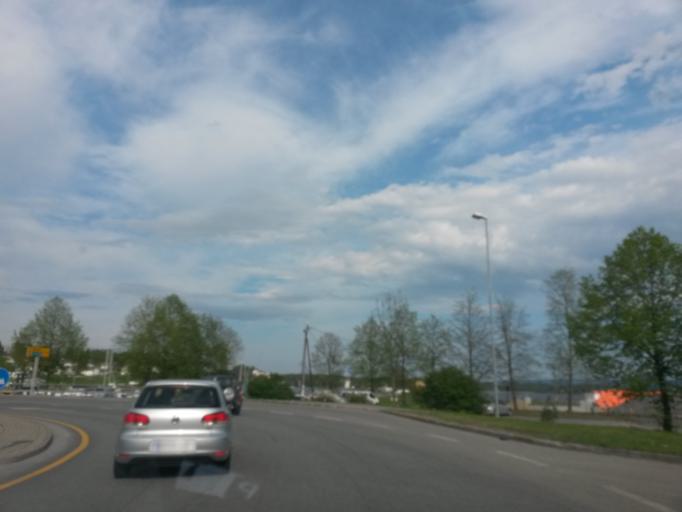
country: NO
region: Akershus
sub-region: Asker
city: Billingstad
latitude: 59.8546
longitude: 10.4918
